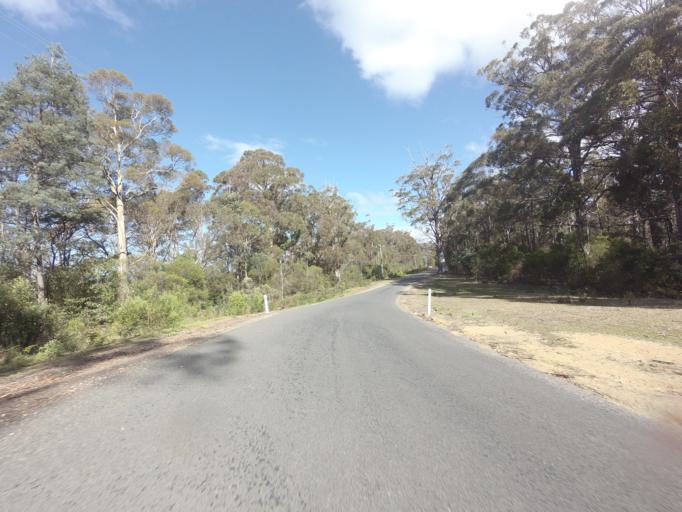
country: AU
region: Tasmania
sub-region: Break O'Day
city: St Helens
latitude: -41.6403
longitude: 148.2428
